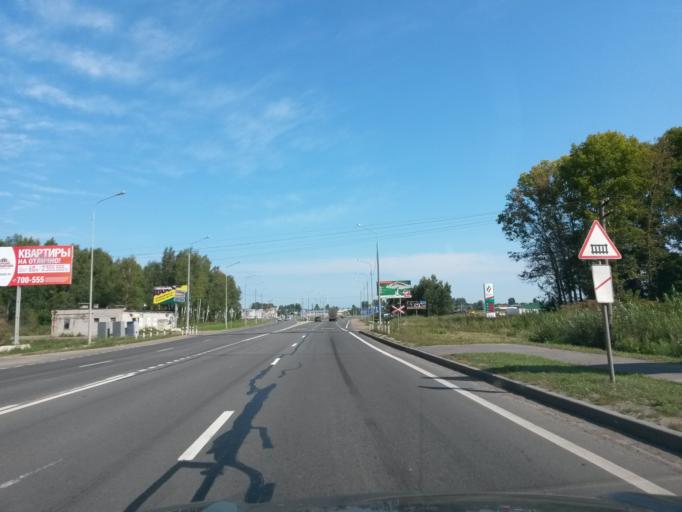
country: RU
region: Jaroslavl
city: Yaroslavl
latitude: 57.6937
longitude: 39.8987
